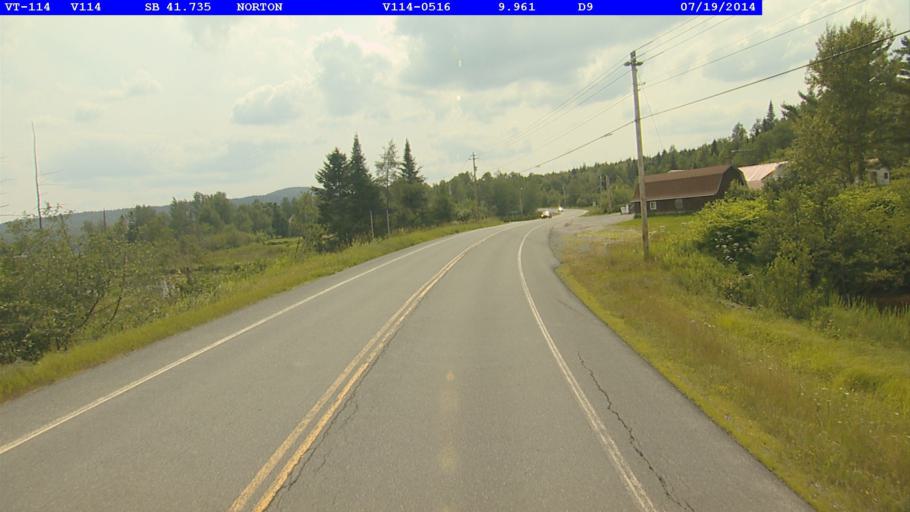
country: CA
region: Quebec
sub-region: Estrie
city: Coaticook
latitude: 44.9992
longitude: -71.7085
